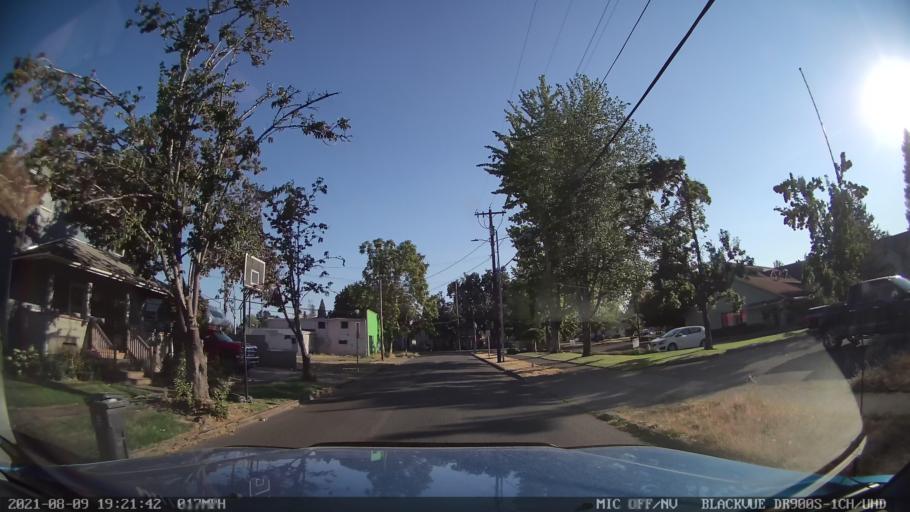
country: US
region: Oregon
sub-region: Marion County
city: Salem
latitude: 44.9400
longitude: -123.0186
